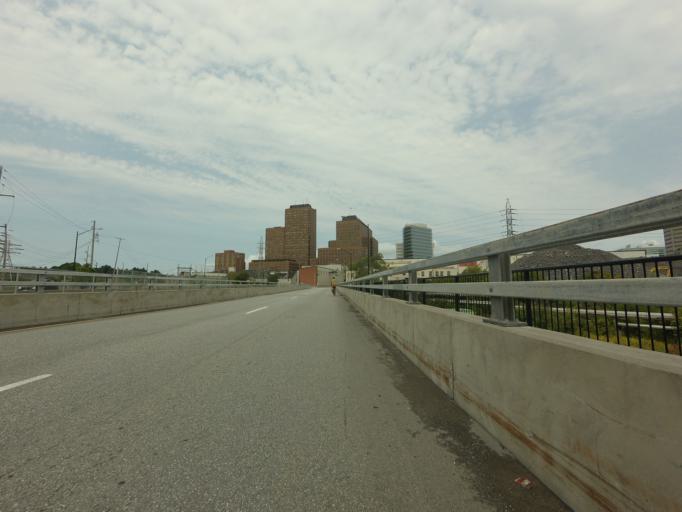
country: CA
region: Ontario
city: Ottawa
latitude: 45.4222
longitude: -75.7189
